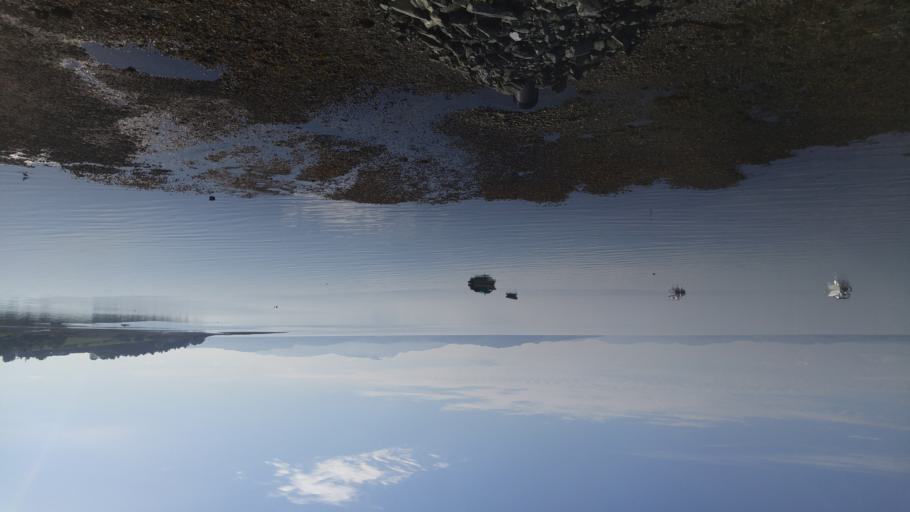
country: NO
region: Sor-Trondelag
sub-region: Malvik
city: Malvik
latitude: 63.4382
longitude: 10.6101
